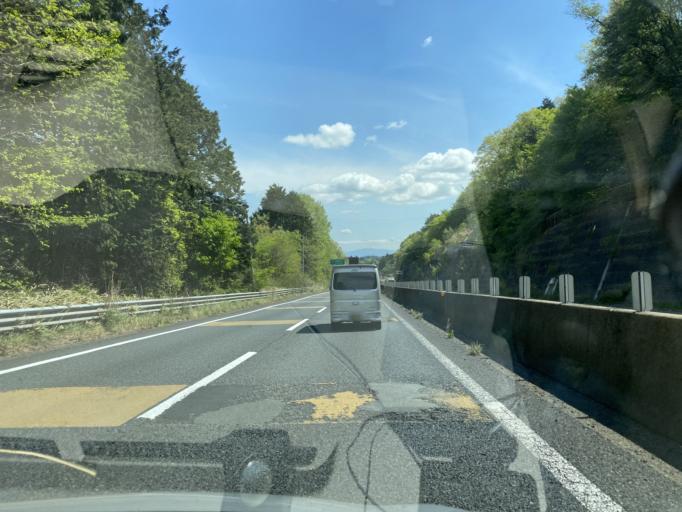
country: JP
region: Mie
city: Nabari
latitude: 34.6474
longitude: 136.0139
